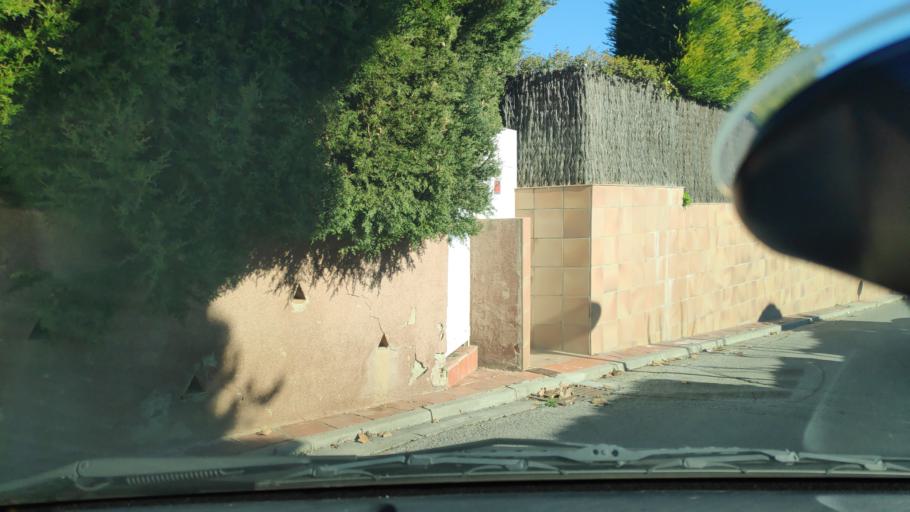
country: ES
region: Catalonia
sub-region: Provincia de Barcelona
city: Sant Quirze del Valles
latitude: 41.5264
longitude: 2.0723
